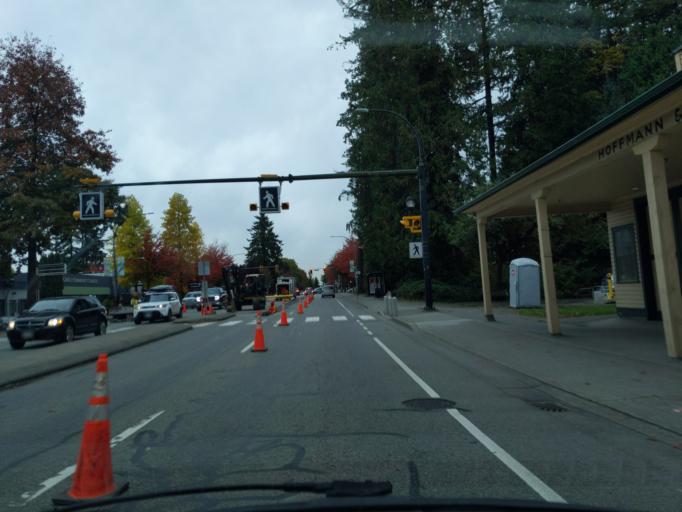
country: CA
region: British Columbia
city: Pitt Meadows
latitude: 49.2258
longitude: -122.6897
